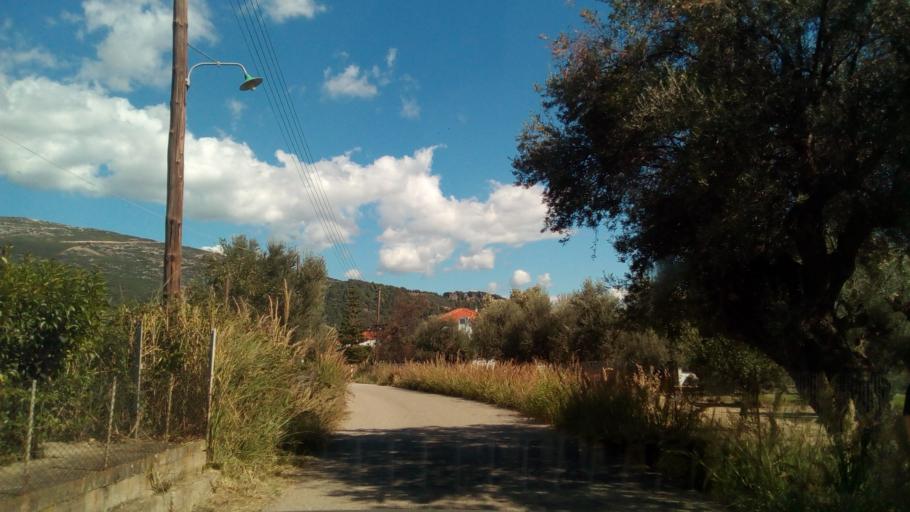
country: GR
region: West Greece
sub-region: Nomos Aitolias kai Akarnanias
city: Nafpaktos
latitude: 38.3863
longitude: 21.8044
